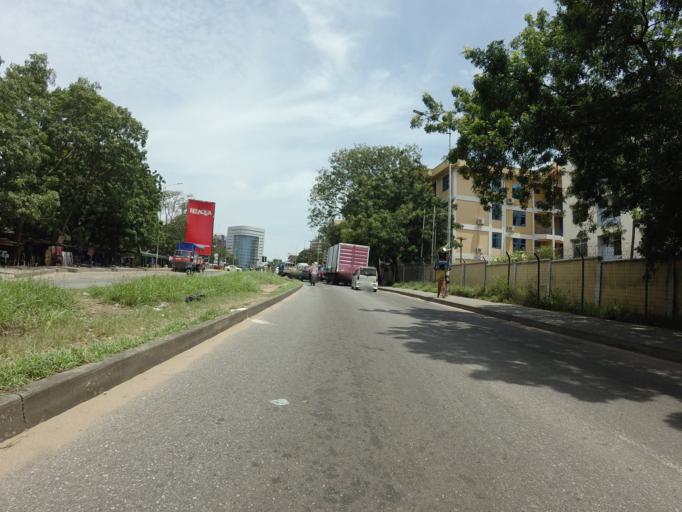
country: GH
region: Greater Accra
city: Accra
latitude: 5.5557
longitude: -0.2063
